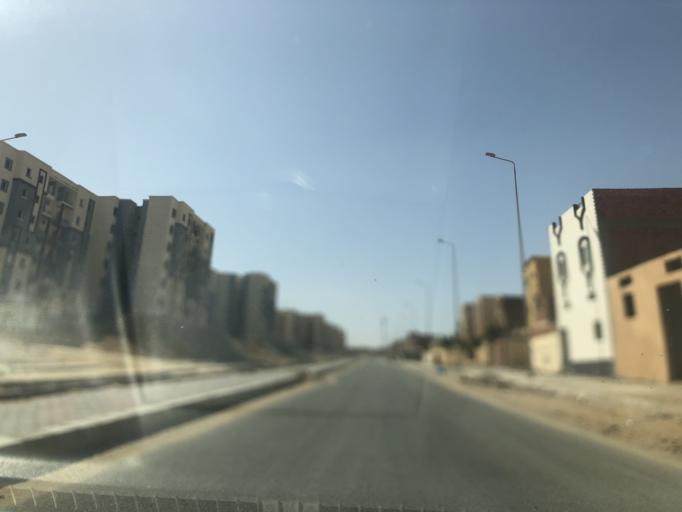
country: EG
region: Al Jizah
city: Madinat Sittah Uktubar
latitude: 29.9326
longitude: 30.9841
